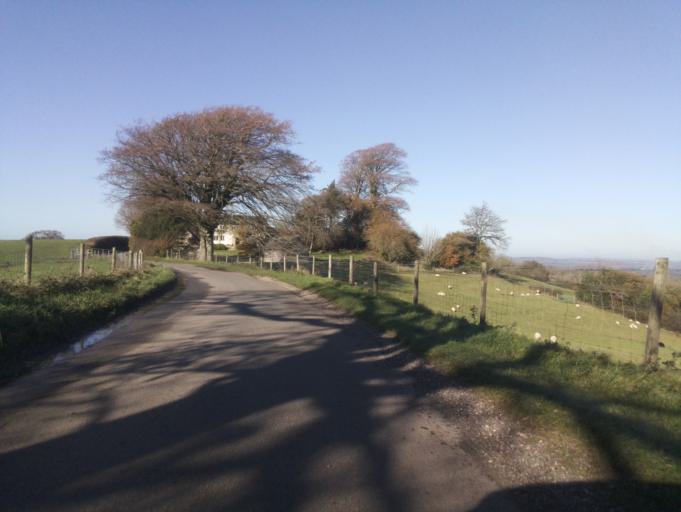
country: GB
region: England
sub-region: Dorset
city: Sherborne
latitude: 50.8510
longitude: -2.5050
